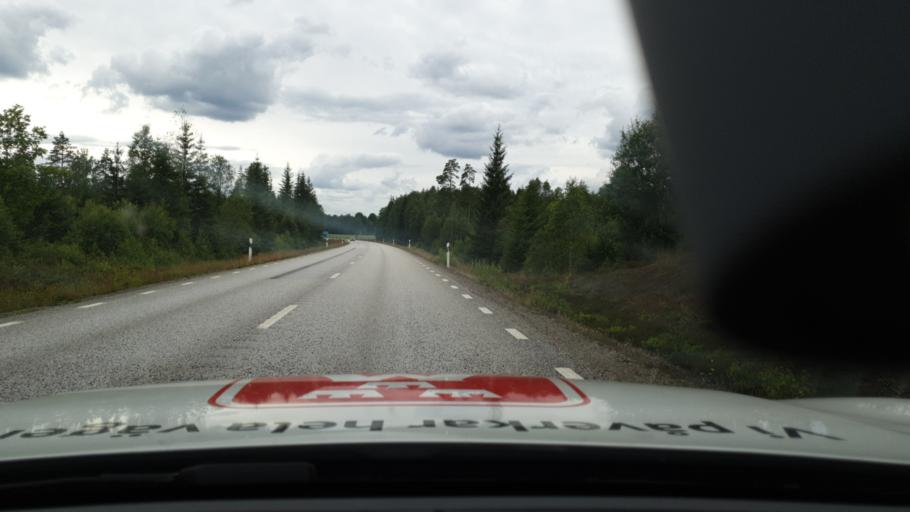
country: SE
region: Joenkoeping
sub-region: Gnosjo Kommun
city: Hillerstorp
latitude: 57.2892
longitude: 13.8350
